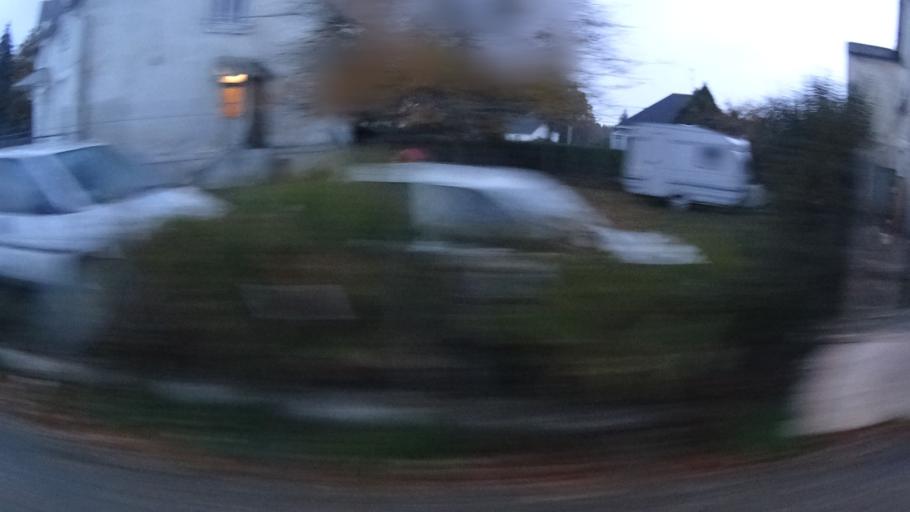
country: FR
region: Pays de la Loire
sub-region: Departement de la Loire-Atlantique
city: Saint-Nicolas-de-Redon
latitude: 47.6613
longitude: -2.0660
